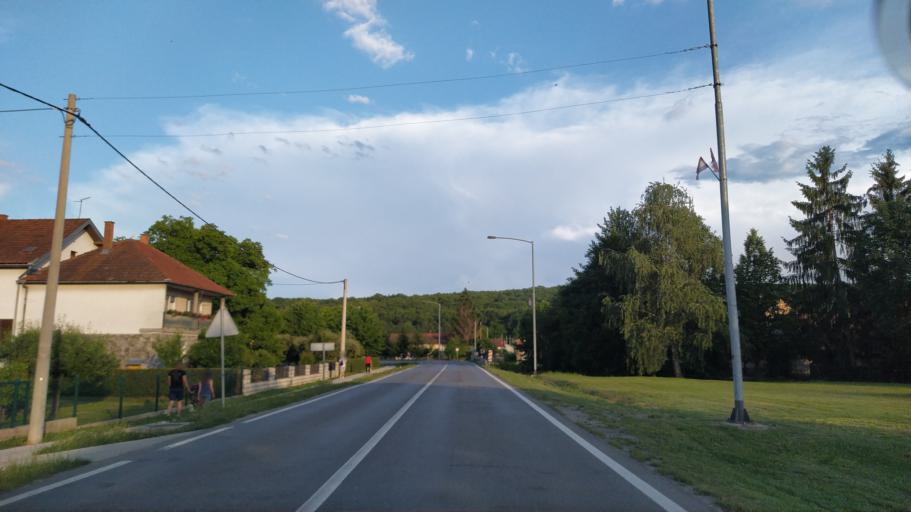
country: HR
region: Osjecko-Baranjska
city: Martin
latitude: 45.4928
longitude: 18.0221
